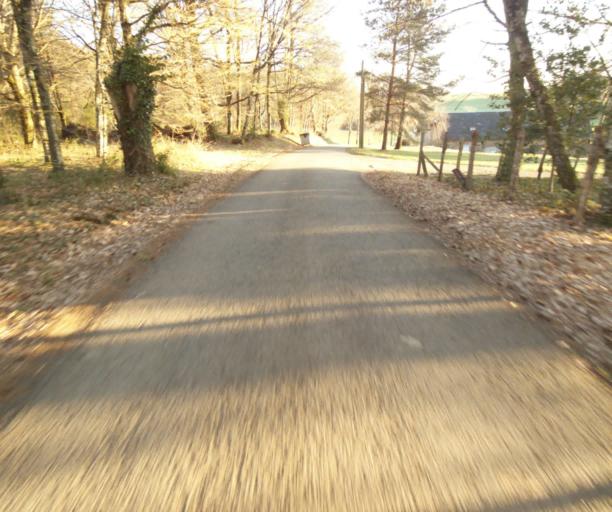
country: FR
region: Limousin
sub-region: Departement de la Correze
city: Seilhac
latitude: 45.3474
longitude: 1.7141
